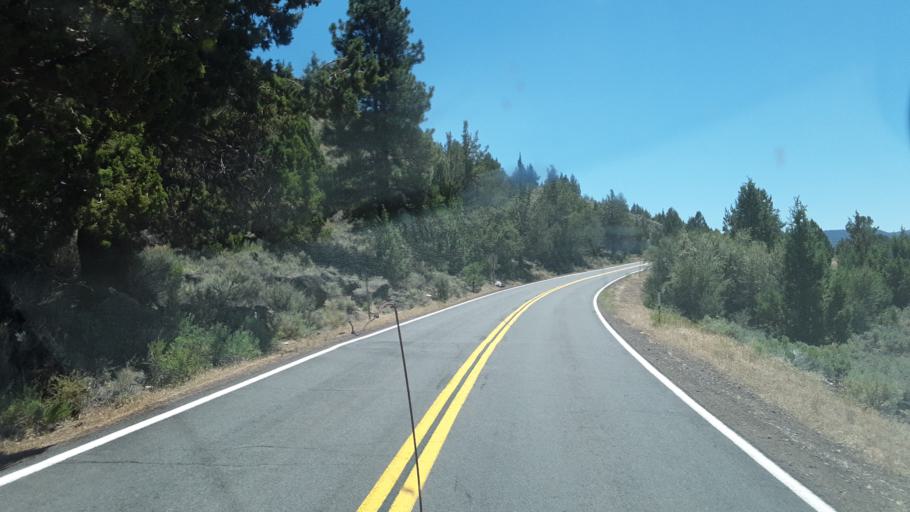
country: US
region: California
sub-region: Lassen County
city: Susanville
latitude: 40.6586
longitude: -120.6567
